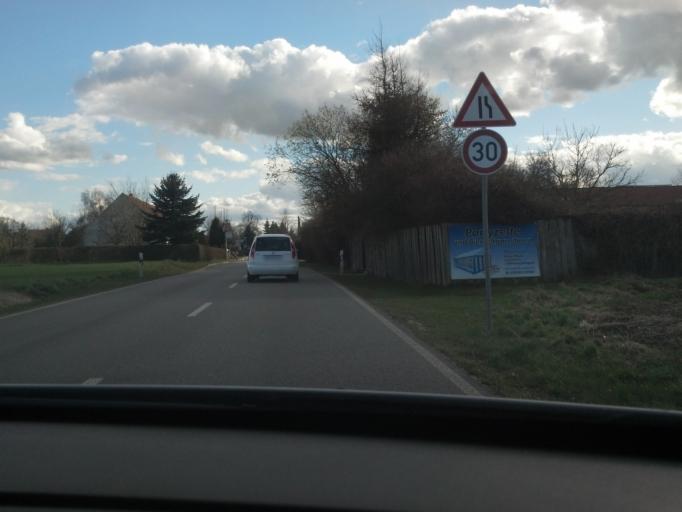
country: DE
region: Mecklenburg-Vorpommern
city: Burg Stargard
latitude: 53.5223
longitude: 13.3196
